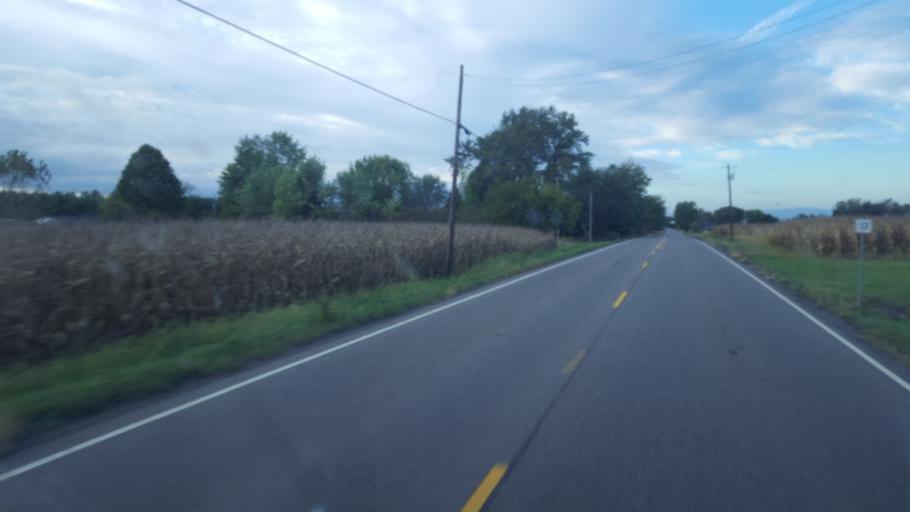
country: US
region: Ohio
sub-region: Licking County
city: Utica
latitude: 40.2398
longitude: -82.5190
